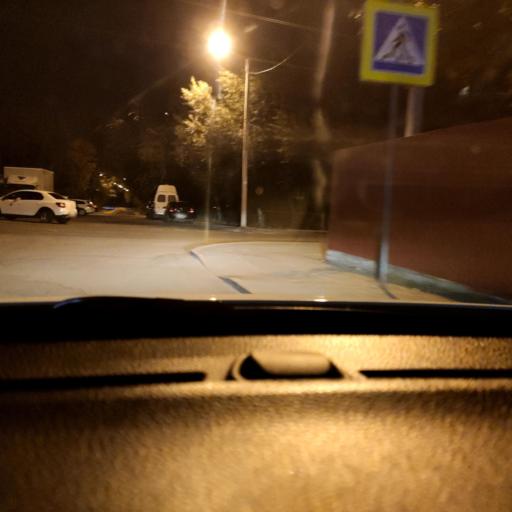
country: RU
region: Voronezj
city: Voronezh
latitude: 51.6883
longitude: 39.1976
